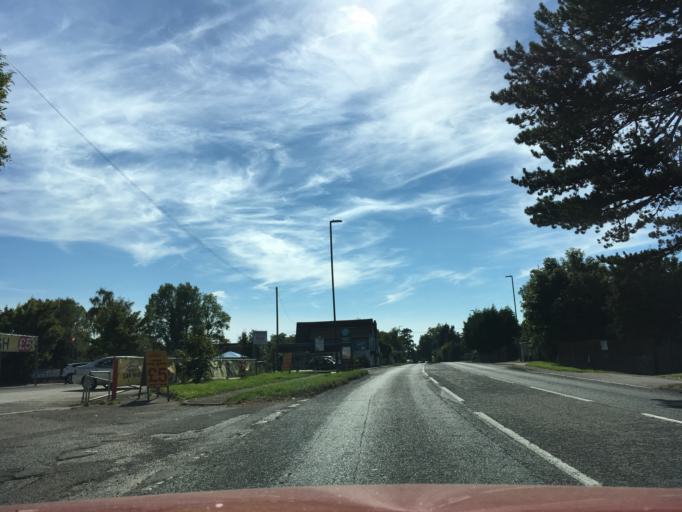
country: GB
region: England
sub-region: South Gloucestershire
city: Alveston
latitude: 51.5810
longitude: -2.5358
